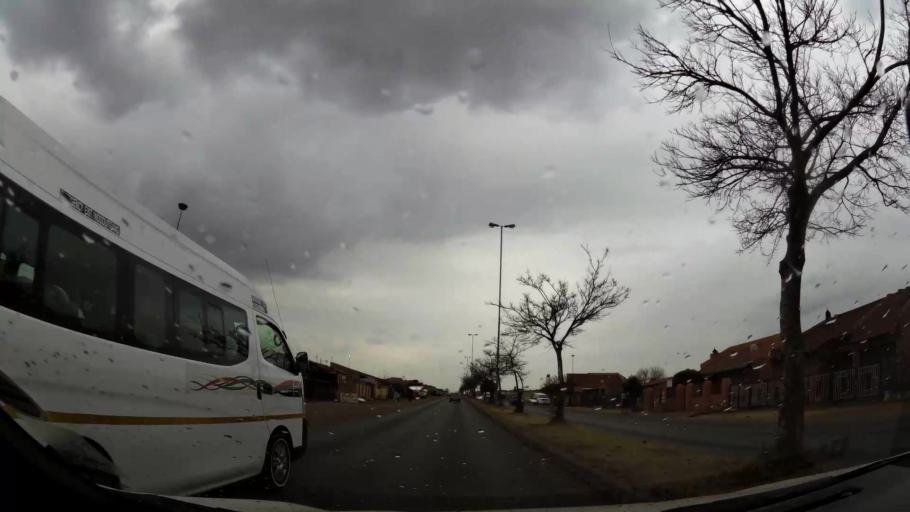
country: ZA
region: Gauteng
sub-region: Ekurhuleni Metropolitan Municipality
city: Germiston
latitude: -26.3394
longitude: 28.1497
